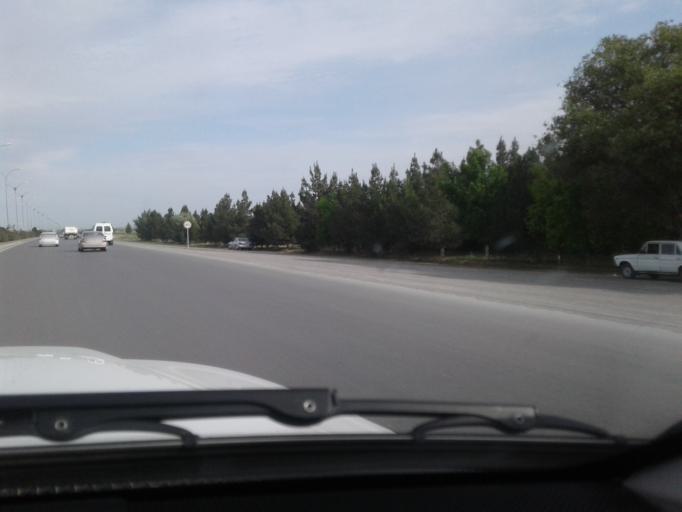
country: TM
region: Ahal
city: Abadan
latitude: 38.1434
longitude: 57.9948
